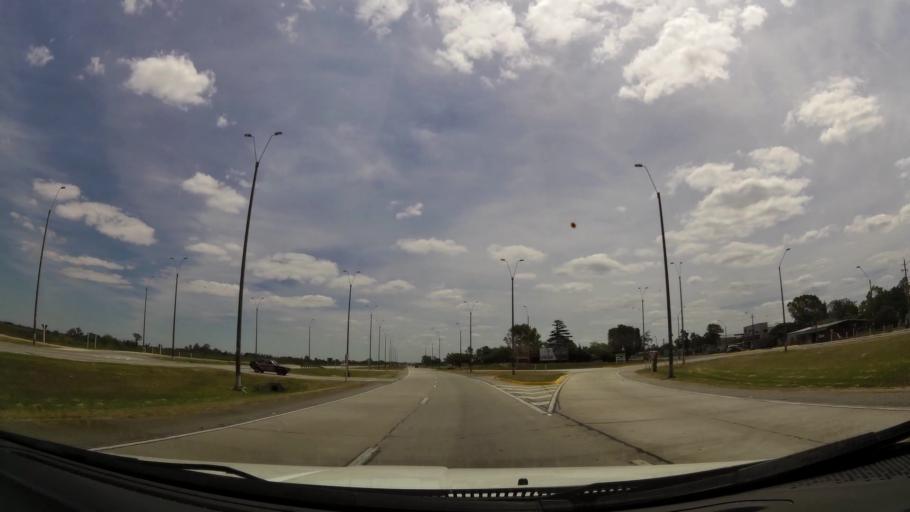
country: UY
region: San Jose
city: Delta del Tigre
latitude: -34.7680
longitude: -56.3920
